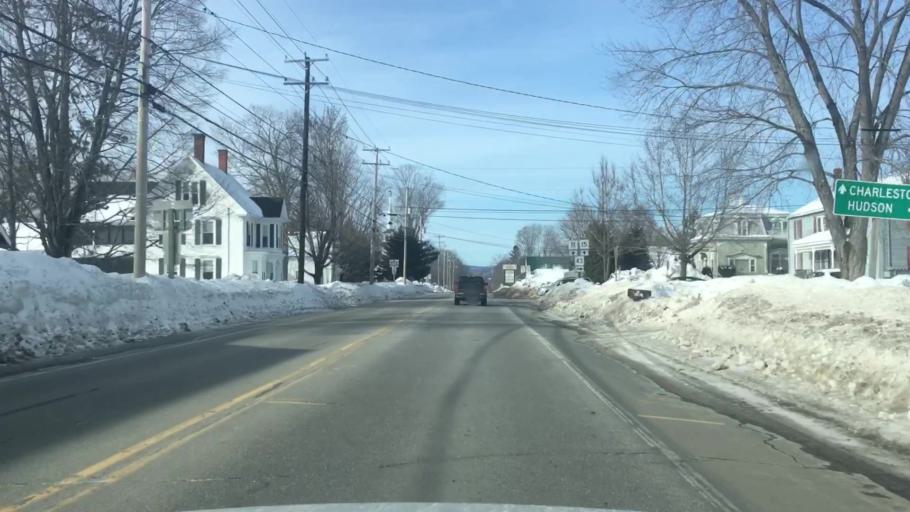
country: US
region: Maine
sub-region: Penobscot County
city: Charleston
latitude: 45.0042
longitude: -69.0237
